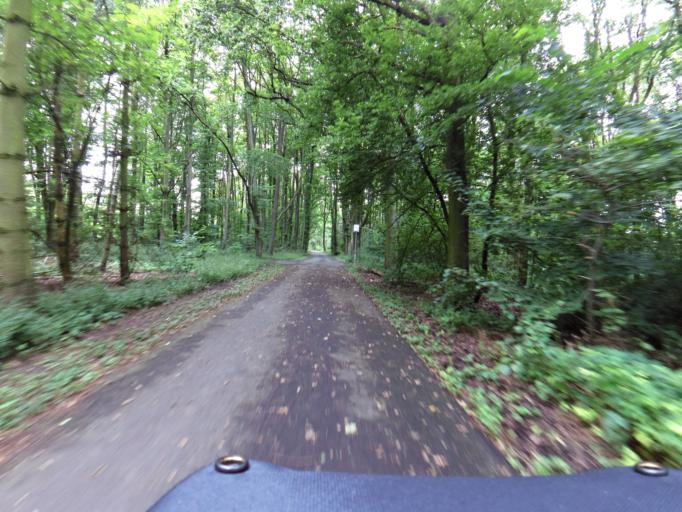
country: NL
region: South Holland
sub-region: Gemeente Spijkenisse
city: Spijkenisse
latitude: 51.8694
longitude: 4.3397
